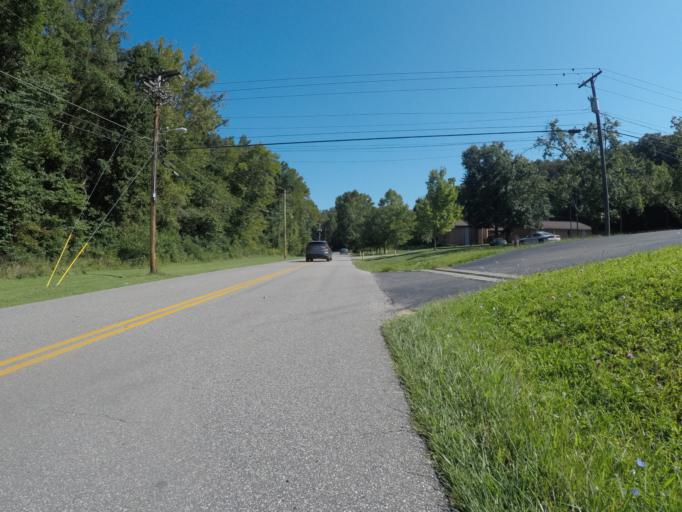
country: US
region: Kentucky
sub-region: Greenup County
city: Russell
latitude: 38.5101
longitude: -82.6948
